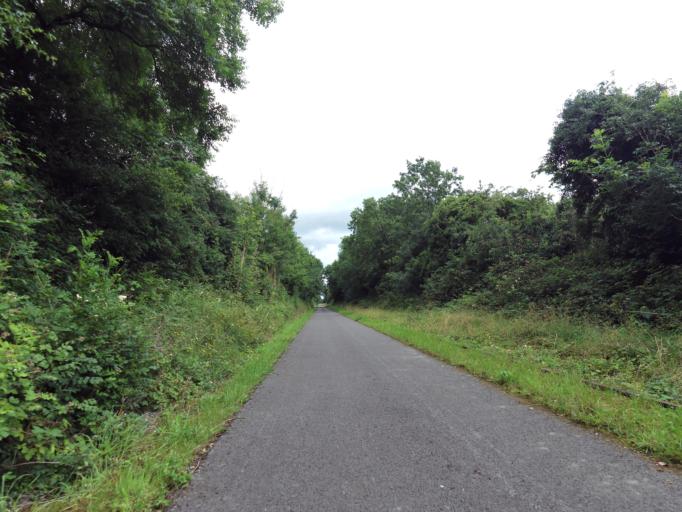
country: IE
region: Leinster
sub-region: An Iarmhi
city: An Muileann gCearr
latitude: 53.5006
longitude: -7.4353
